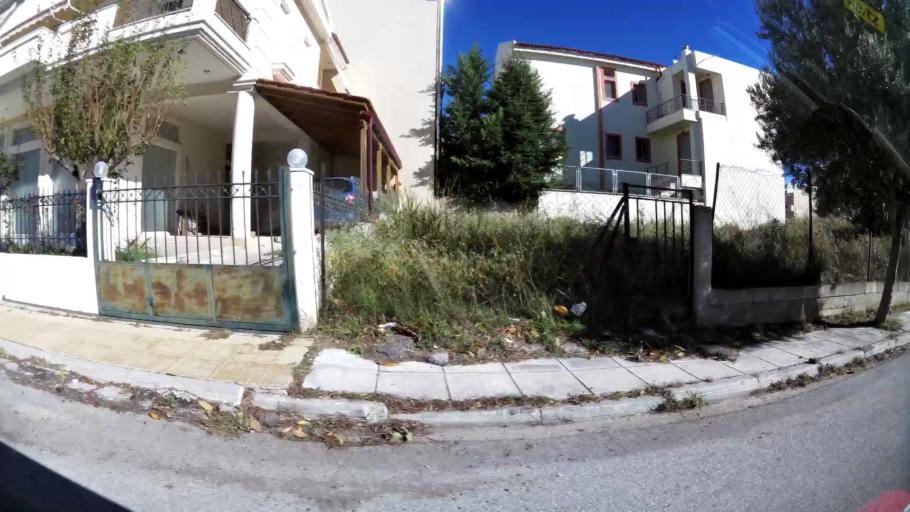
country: GR
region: Attica
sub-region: Nomarchia Anatolikis Attikis
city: Gerakas
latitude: 38.0169
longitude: 23.8558
